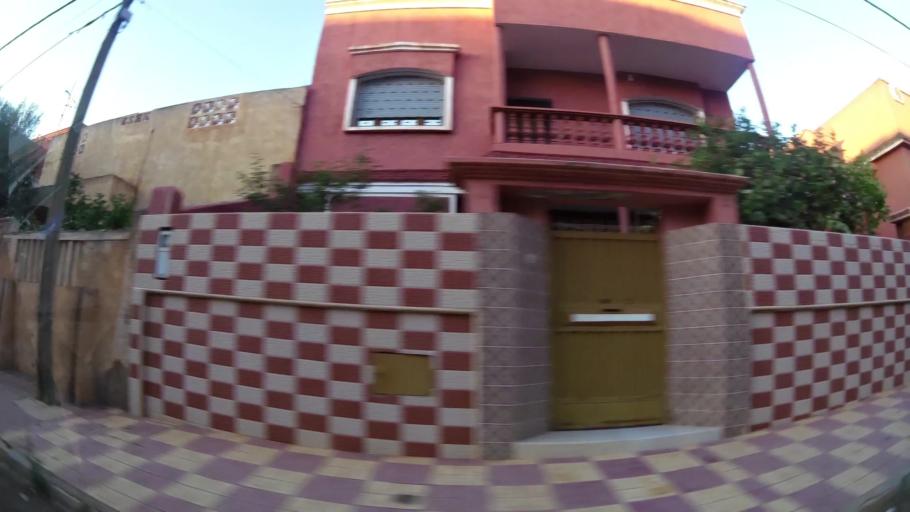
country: MA
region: Oriental
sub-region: Berkane-Taourirt
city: Berkane
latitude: 34.9141
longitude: -2.3163
